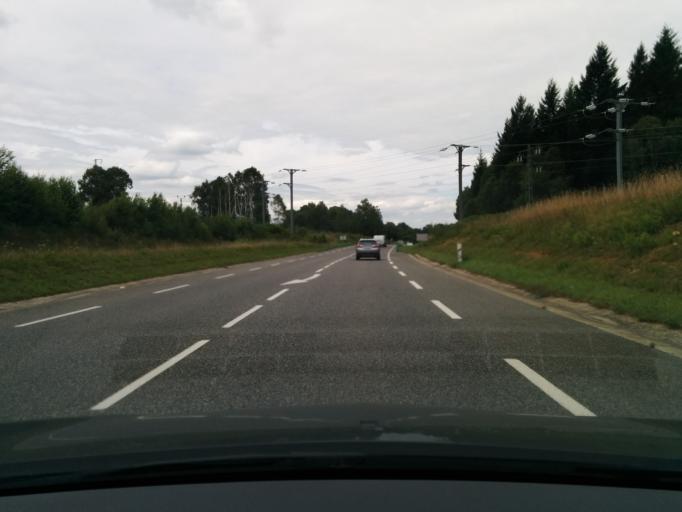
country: FR
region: Midi-Pyrenees
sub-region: Departement des Hautes-Pyrenees
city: La Barthe-de-Neste
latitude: 43.0757
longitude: 0.3618
